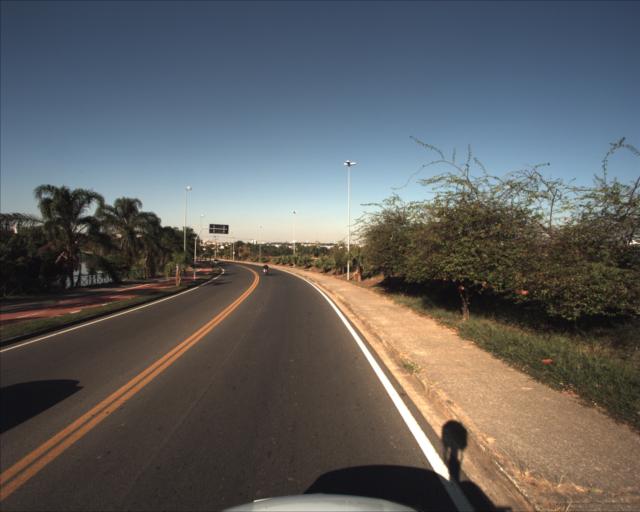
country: BR
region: Sao Paulo
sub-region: Sorocaba
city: Sorocaba
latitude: -23.4703
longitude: -47.4512
